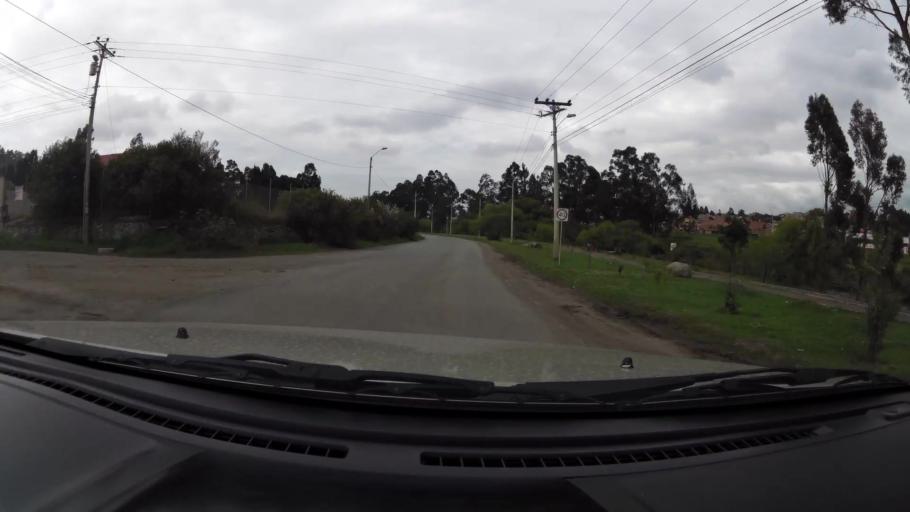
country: EC
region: Azuay
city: Cuenca
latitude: -2.8935
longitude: -78.9639
